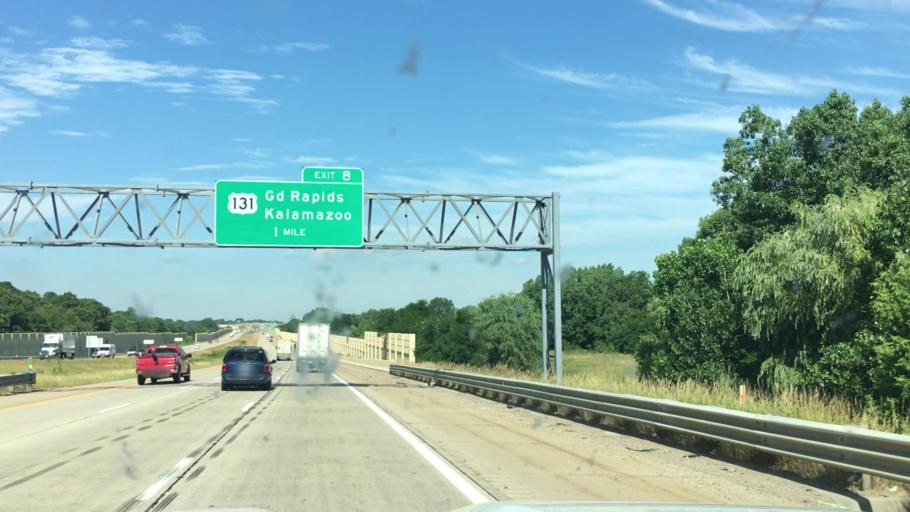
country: US
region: Michigan
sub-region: Kent County
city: Cutlerville
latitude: 42.8490
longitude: -85.6456
